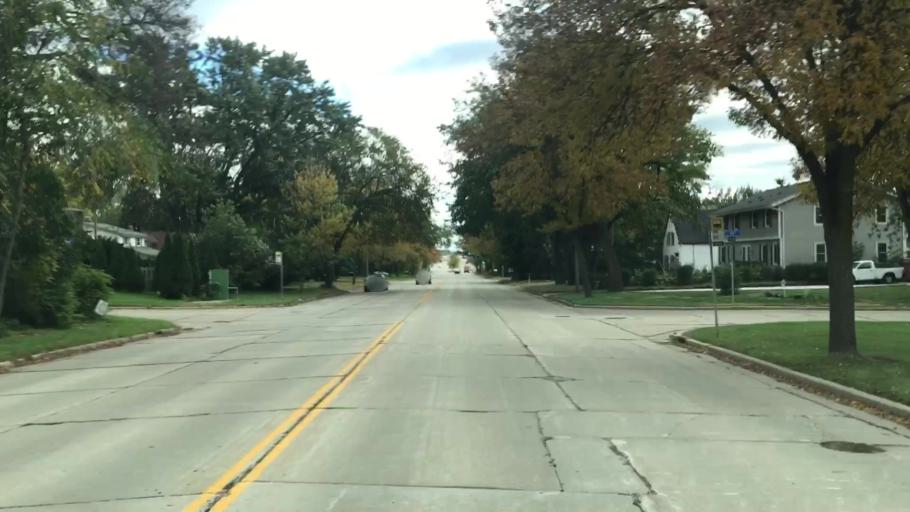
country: US
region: Wisconsin
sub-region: Waukesha County
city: Elm Grove
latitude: 43.0455
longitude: -88.0602
